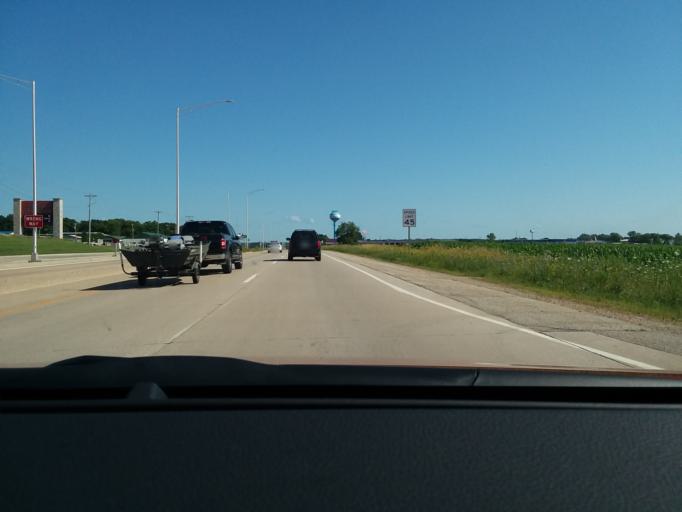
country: US
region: Wisconsin
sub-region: Dane County
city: Windsor
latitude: 43.1648
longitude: -89.3243
